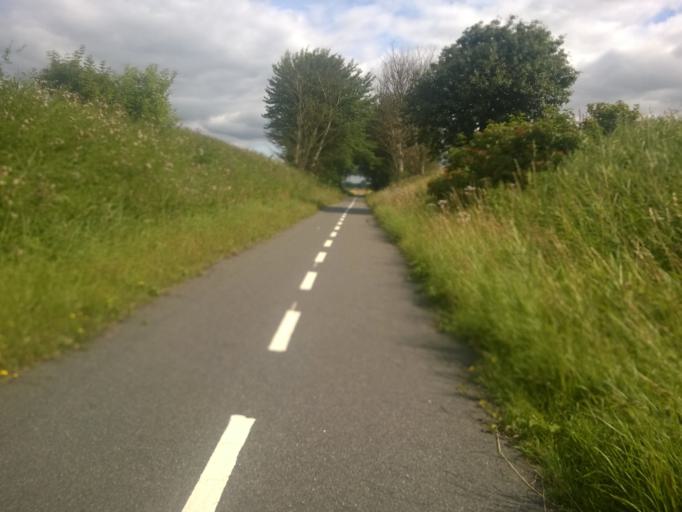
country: SE
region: Skane
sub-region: Kristianstads Kommun
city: Kristianstad
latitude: 56.0634
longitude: 14.1872
